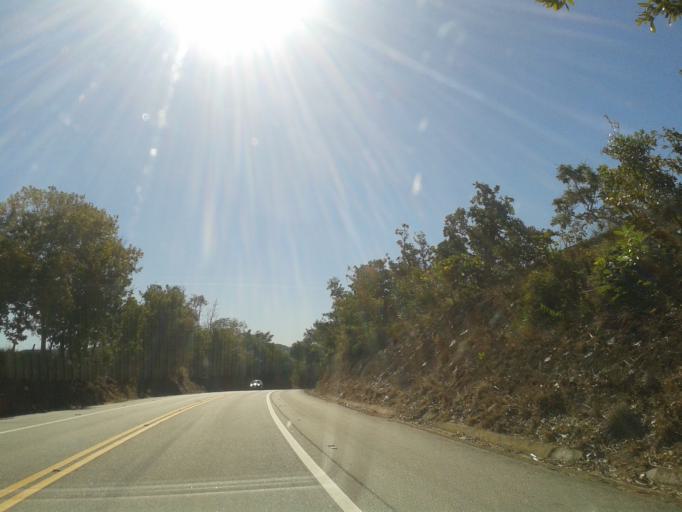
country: BR
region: Goias
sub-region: Itapuranga
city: Itapuranga
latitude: -15.6143
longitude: -50.2459
